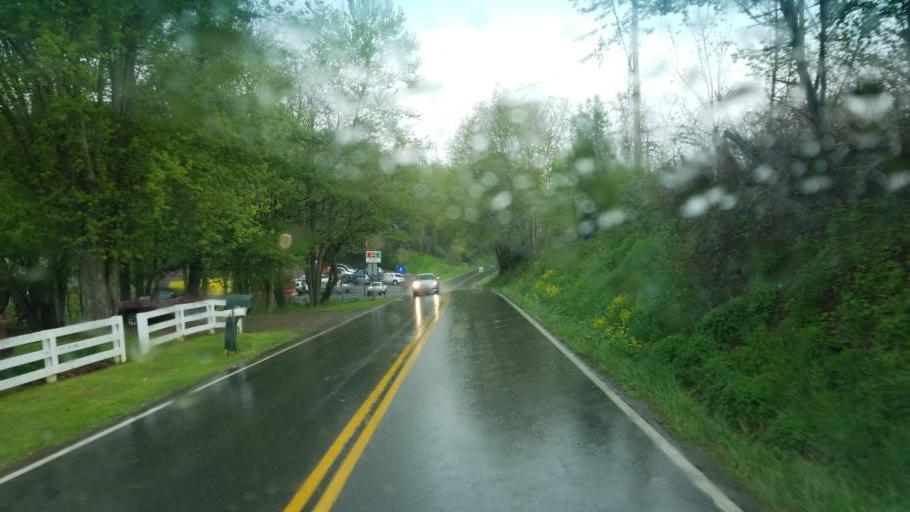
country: US
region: Virginia
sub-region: Smyth County
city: Adwolf
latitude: 36.8030
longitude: -81.5775
